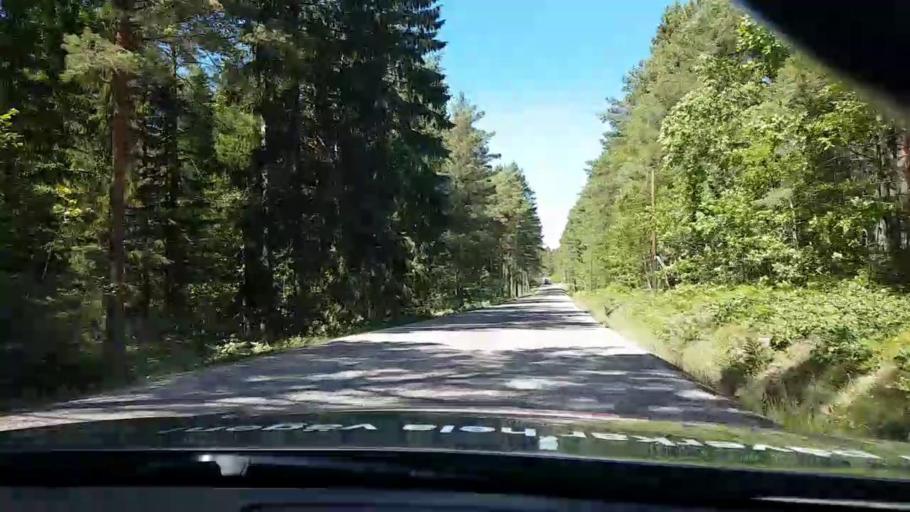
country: SE
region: Kalmar
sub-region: Vasterviks Kommun
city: Vaestervik
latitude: 57.9103
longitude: 16.6442
